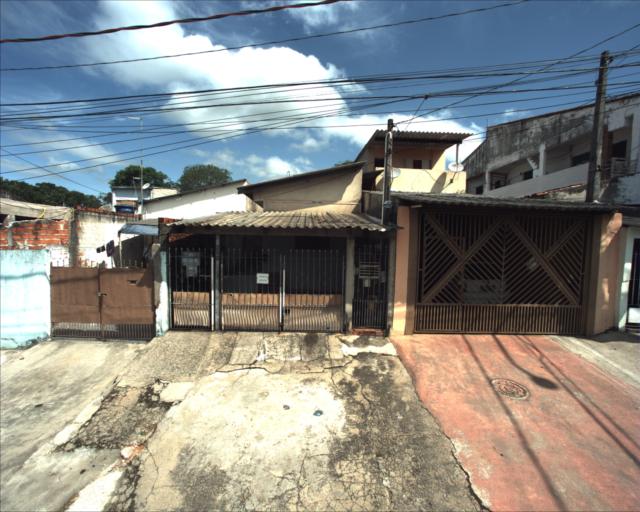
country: BR
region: Sao Paulo
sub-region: Sorocaba
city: Sorocaba
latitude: -23.3944
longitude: -47.3777
